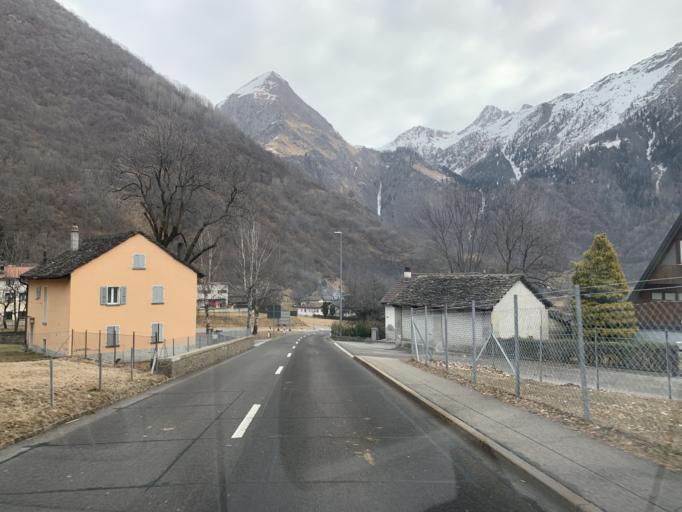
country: CH
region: Ticino
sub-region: Blenio District
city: Cancori
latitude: 46.5273
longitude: 8.9241
